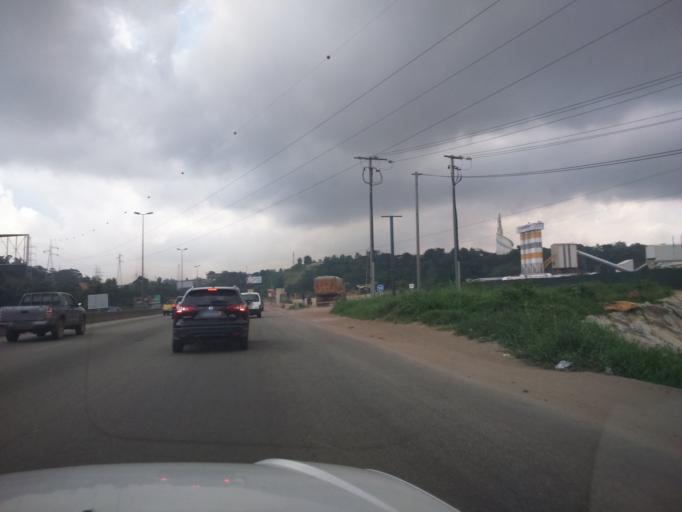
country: CI
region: Lagunes
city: Abidjan
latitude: 5.3595
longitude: -4.0448
